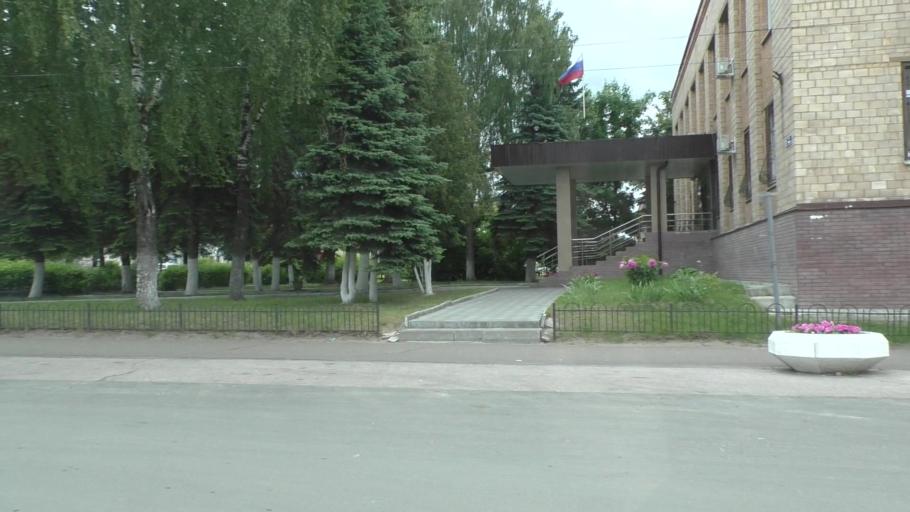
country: RU
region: Moskovskaya
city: Yegor'yevsk
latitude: 55.3721
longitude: 39.0550
